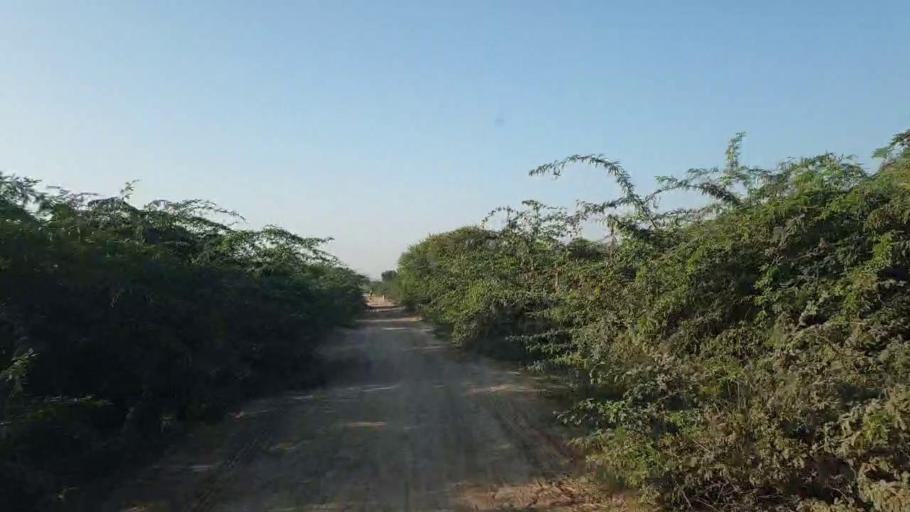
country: PK
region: Sindh
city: Badin
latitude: 24.6153
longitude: 68.7865
